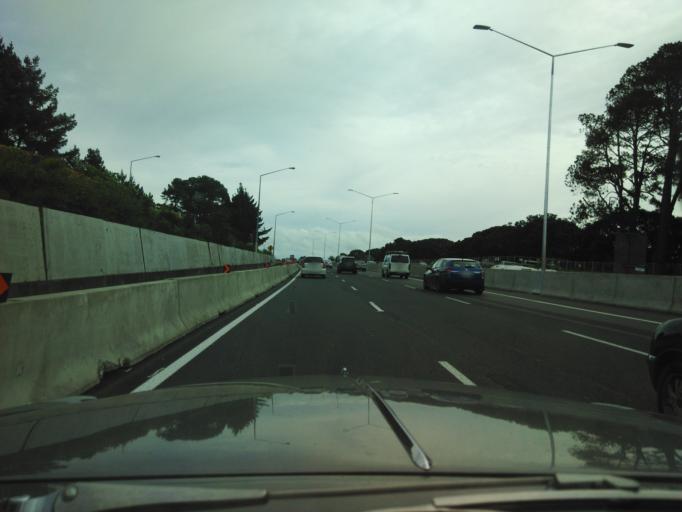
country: NZ
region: Auckland
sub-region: Auckland
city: Auckland
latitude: -36.8689
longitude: 174.7250
